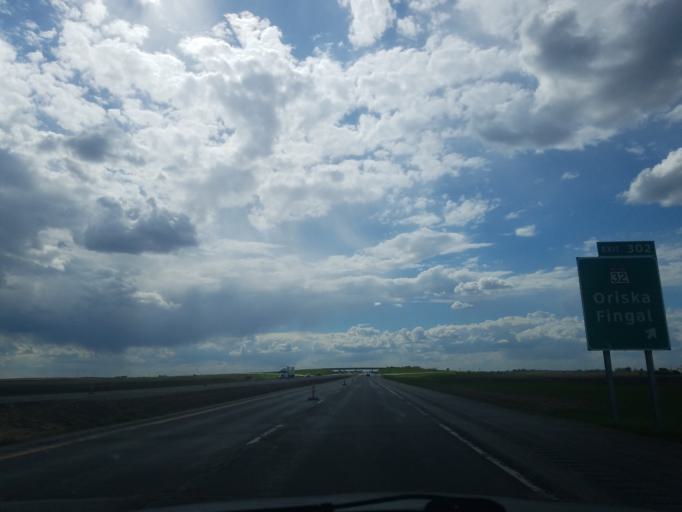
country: US
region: North Dakota
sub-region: Barnes County
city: Valley City
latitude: 46.9201
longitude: -97.7783
